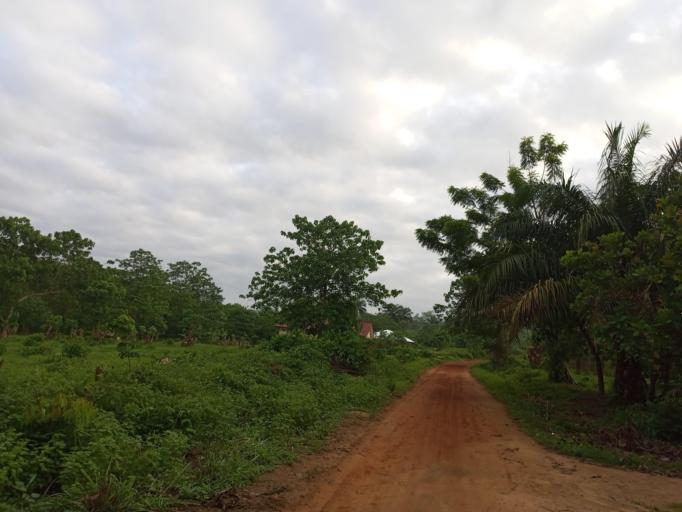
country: SL
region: Eastern Province
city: Pendembu
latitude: 8.1148
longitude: -10.6912
